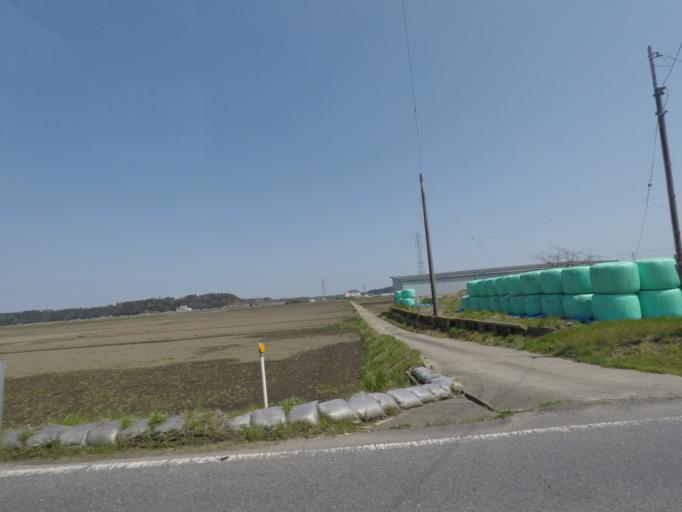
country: JP
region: Chiba
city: Yokaichiba
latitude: 35.6791
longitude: 140.4654
